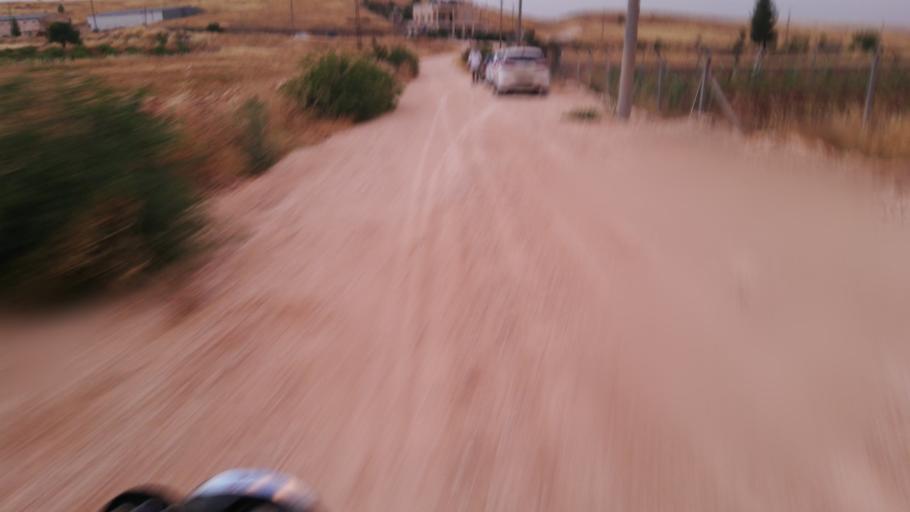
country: TR
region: Mardin
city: Kindirip
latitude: 37.4596
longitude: 41.2212
